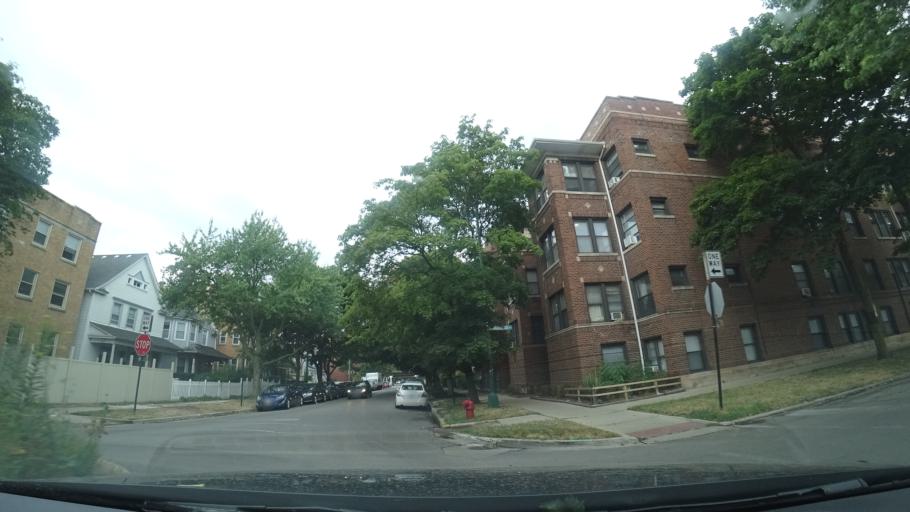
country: US
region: Illinois
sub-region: Cook County
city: Evanston
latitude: 41.9944
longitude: -87.6733
